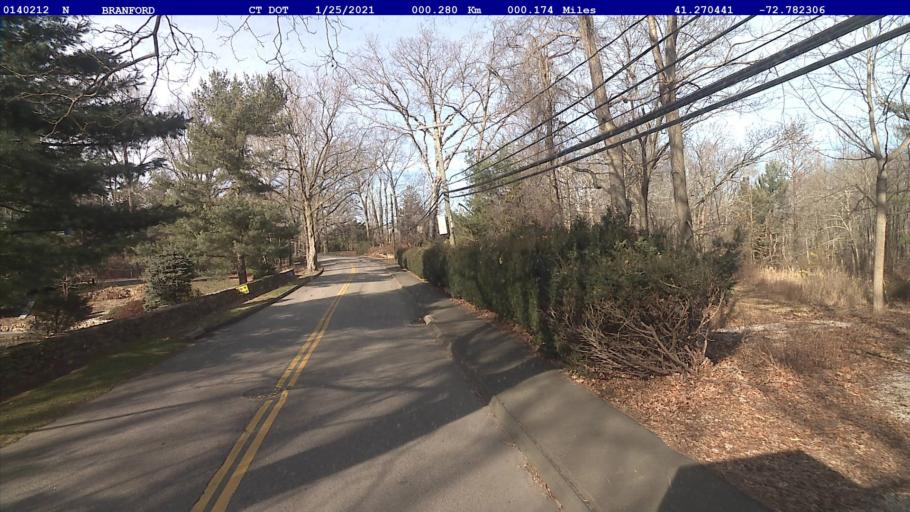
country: US
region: Connecticut
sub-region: New Haven County
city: Branford Center
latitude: 41.2705
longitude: -72.7823
